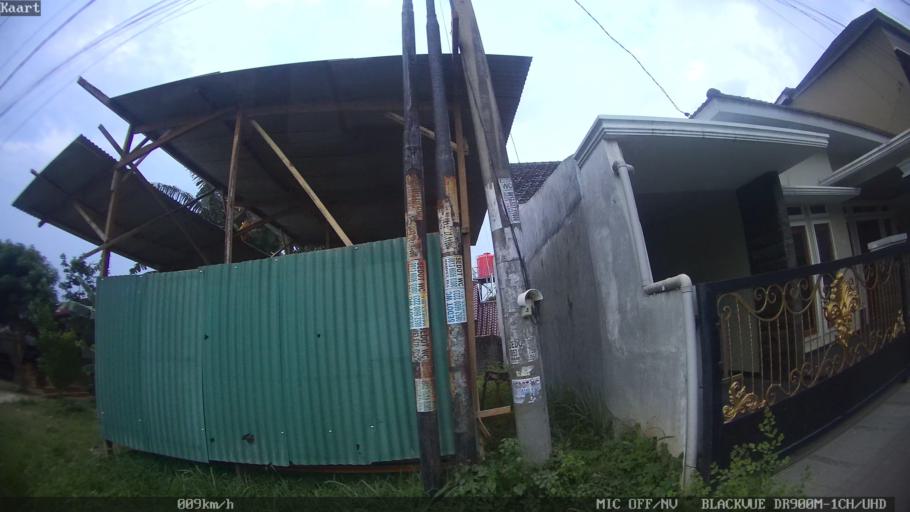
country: ID
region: Lampung
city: Bandarlampung
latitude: -5.4077
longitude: 105.2881
